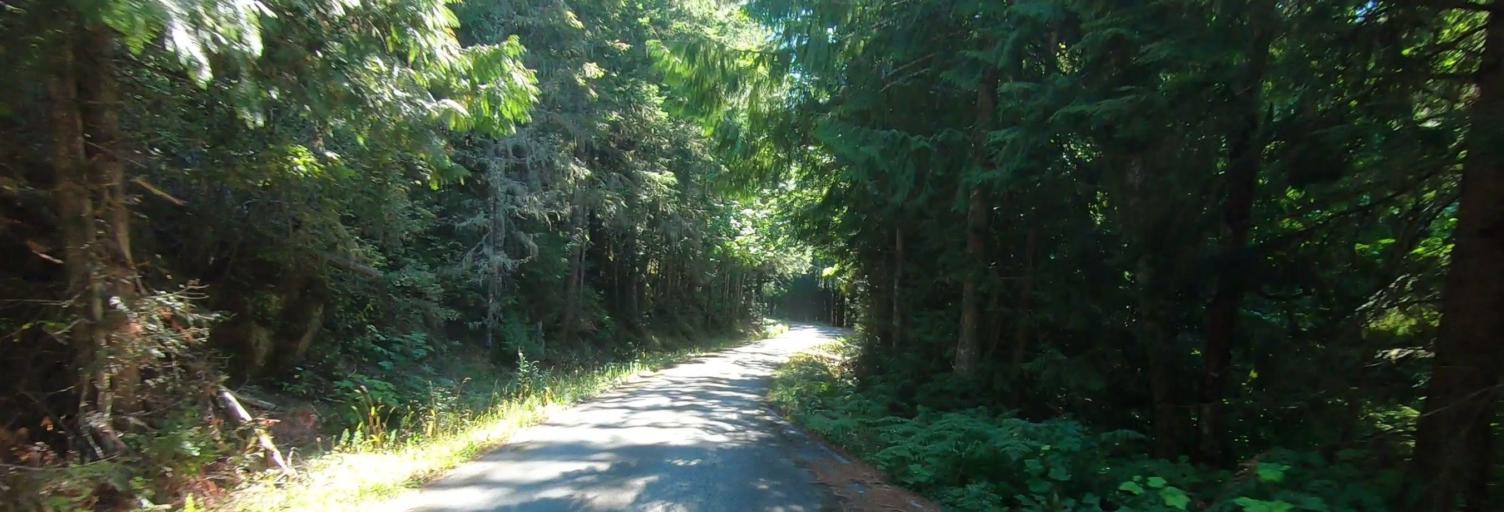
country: US
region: Washington
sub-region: Whatcom County
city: Peaceful Valley
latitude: 48.9056
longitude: -121.9603
